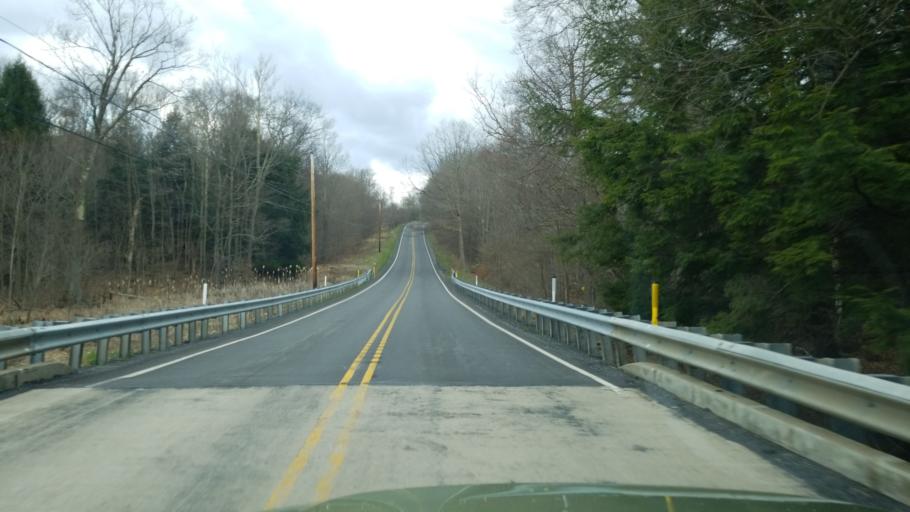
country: US
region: Pennsylvania
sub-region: Clearfield County
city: Curwensville
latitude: 40.8819
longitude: -78.4603
